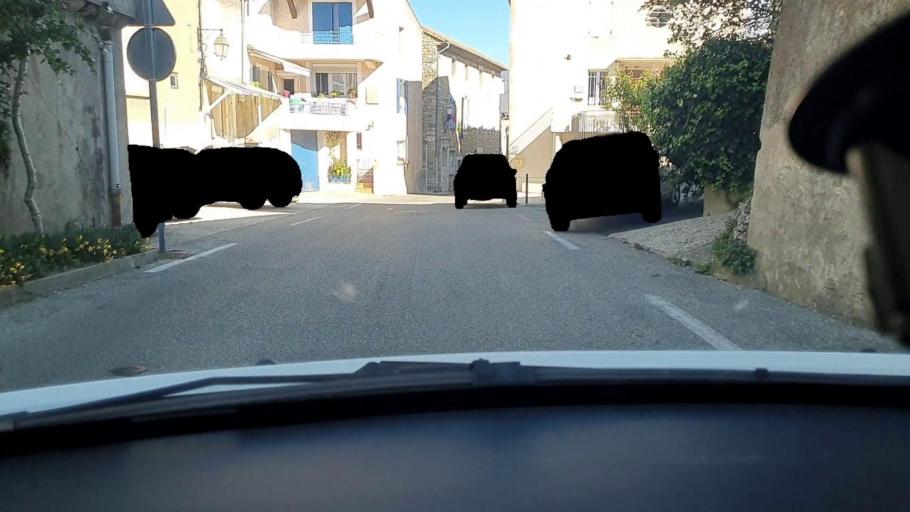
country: FR
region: Languedoc-Roussillon
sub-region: Departement du Gard
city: Saint-Julien-de-Peyrolas
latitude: 44.2873
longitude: 4.5648
